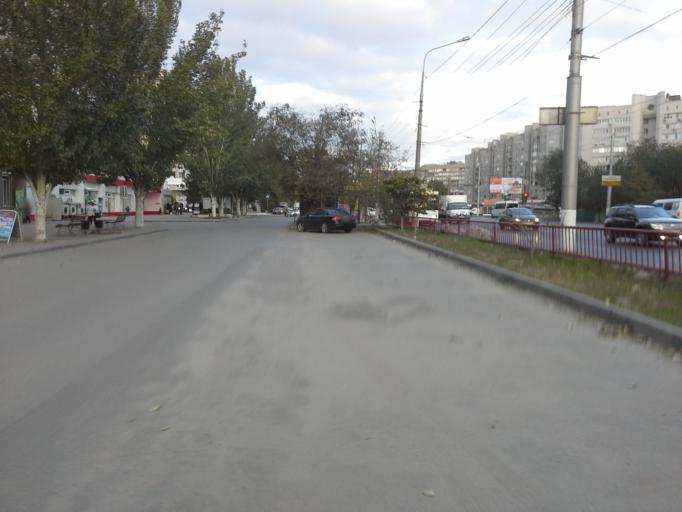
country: RU
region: Volgograd
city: Vodstroy
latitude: 48.8167
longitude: 44.6261
